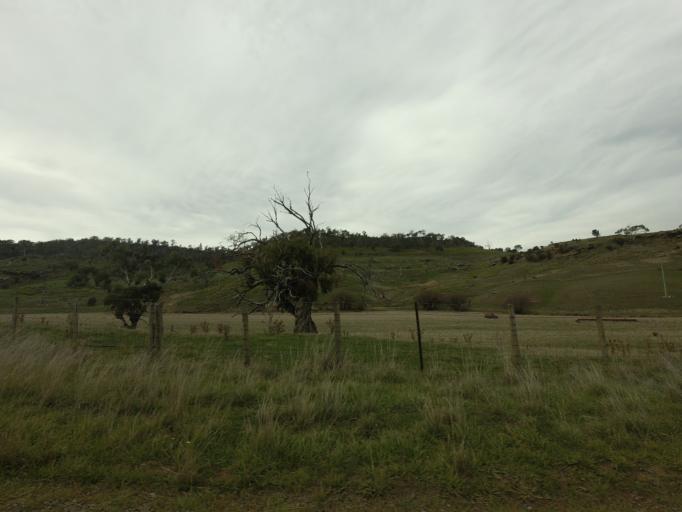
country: AU
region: Tasmania
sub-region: Derwent Valley
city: New Norfolk
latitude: -42.4062
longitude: 146.9208
